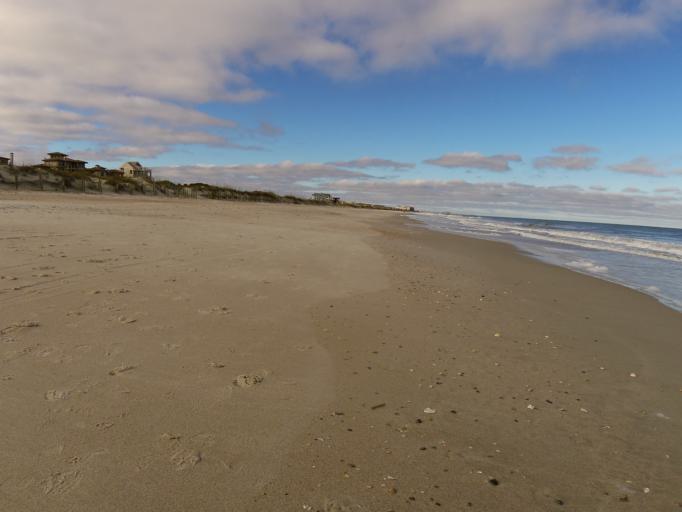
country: US
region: Florida
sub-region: Nassau County
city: Fernandina Beach
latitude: 30.5650
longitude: -81.4427
